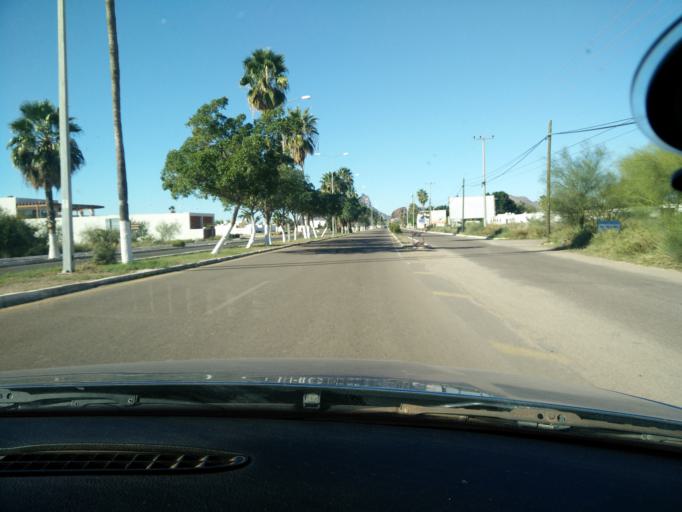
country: MX
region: Sonora
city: Heroica Guaymas
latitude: 27.9666
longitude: -111.0128
